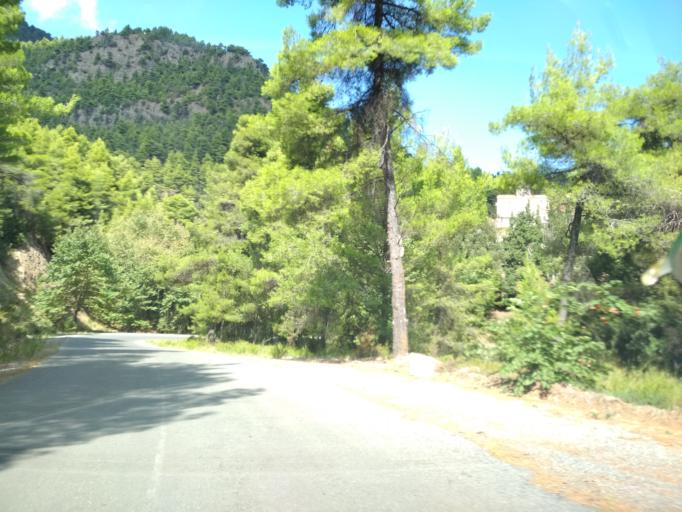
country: GR
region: Central Greece
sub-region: Nomos Evvoias
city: Roviai
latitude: 38.8445
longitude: 23.2828
